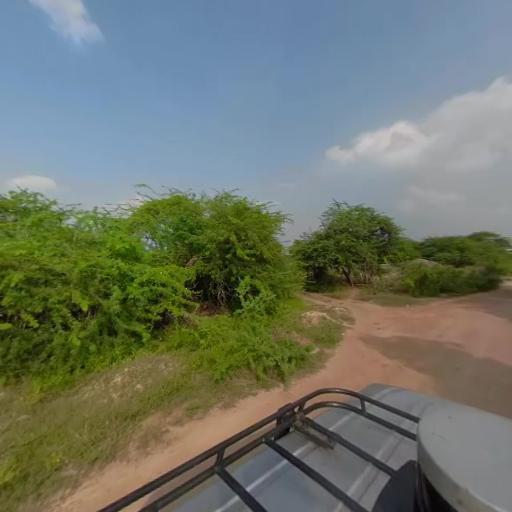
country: IN
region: Telangana
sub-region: Nalgonda
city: Suriapet
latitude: 17.2002
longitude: 79.4880
